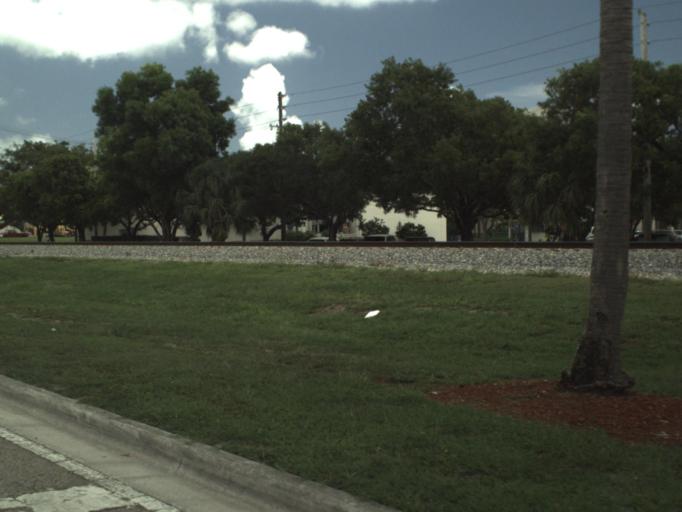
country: US
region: Florida
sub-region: Broward County
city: Pompano Beach
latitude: 26.2302
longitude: -80.1265
